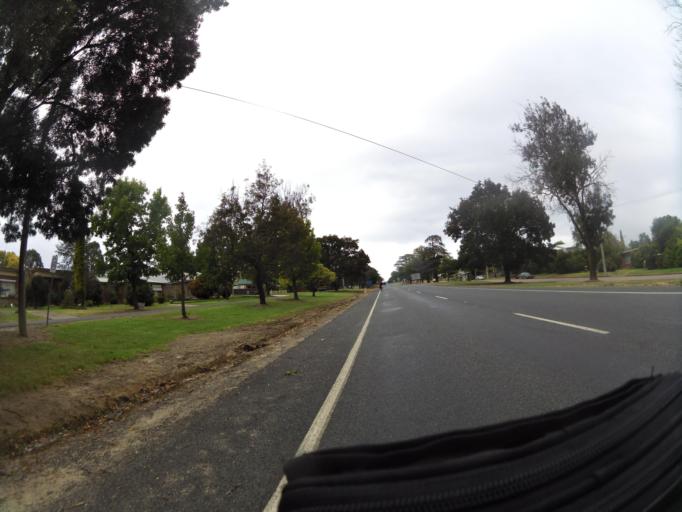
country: AU
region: New South Wales
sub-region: Snowy River
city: Jindabyne
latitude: -36.1892
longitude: 147.9144
